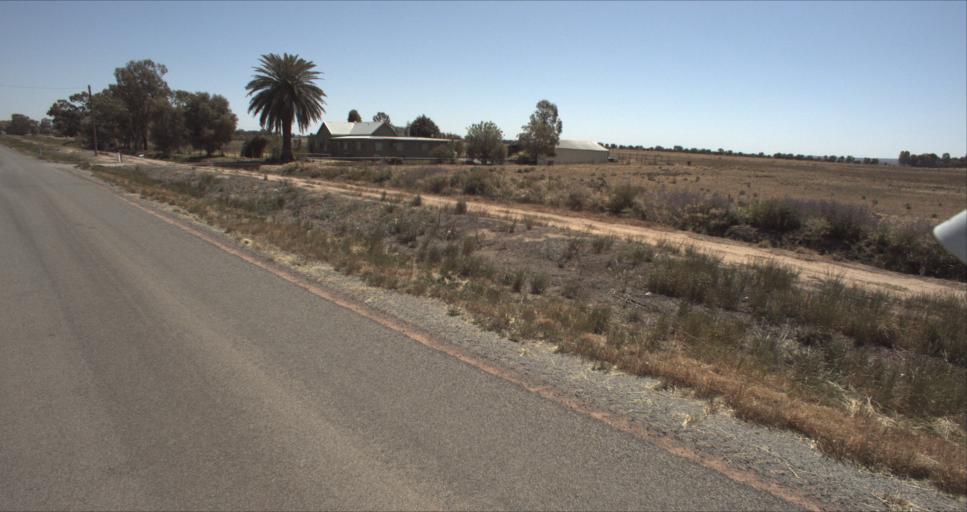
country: AU
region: New South Wales
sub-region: Leeton
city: Leeton
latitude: -34.5283
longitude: 146.4015
